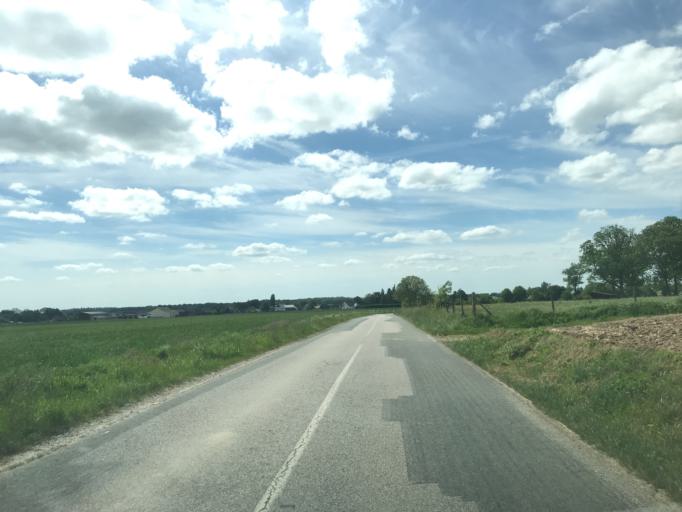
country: FR
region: Haute-Normandie
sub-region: Departement de l'Eure
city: Le Neubourg
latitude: 49.1472
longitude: 0.8450
